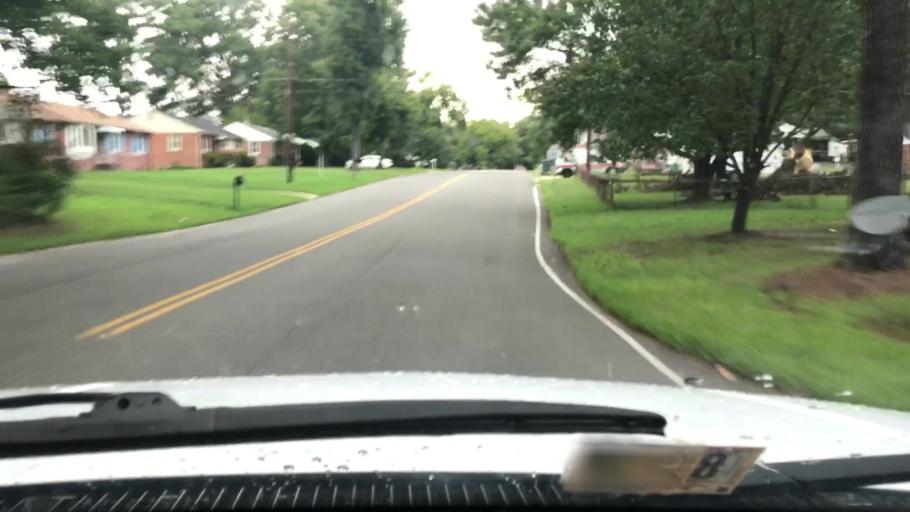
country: US
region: Virginia
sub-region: Henrico County
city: Dumbarton
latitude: 37.5972
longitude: -77.5091
